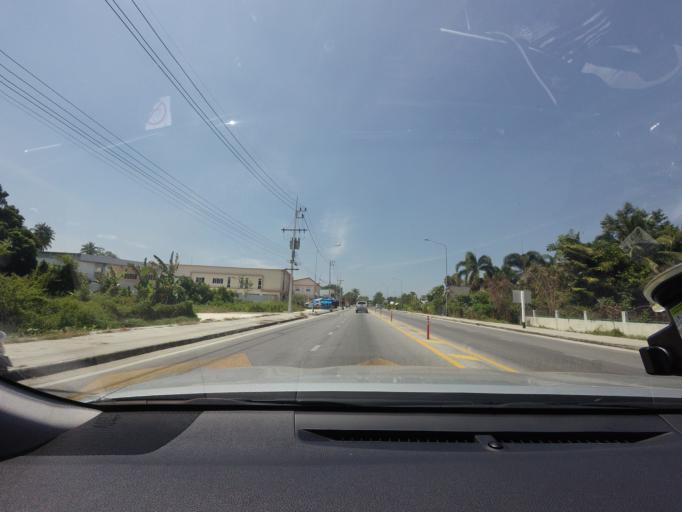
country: TH
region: Narathiwat
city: Narathiwat
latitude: 6.4273
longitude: 101.8172
